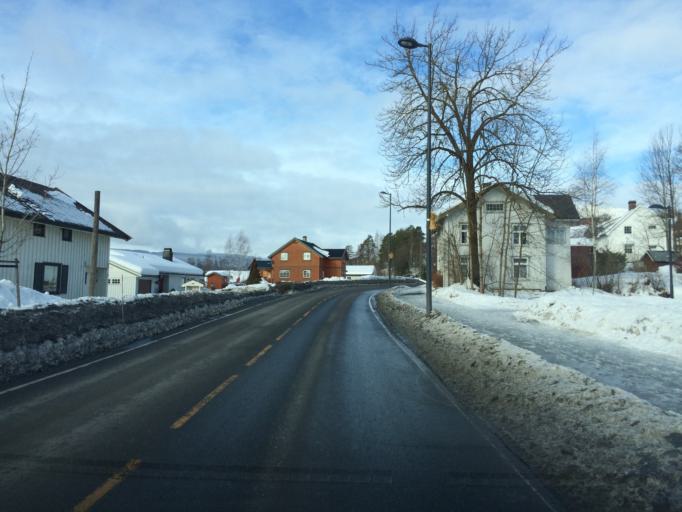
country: NO
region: Oppland
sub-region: Gausdal
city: Segalstad bru
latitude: 61.2167
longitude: 10.2795
